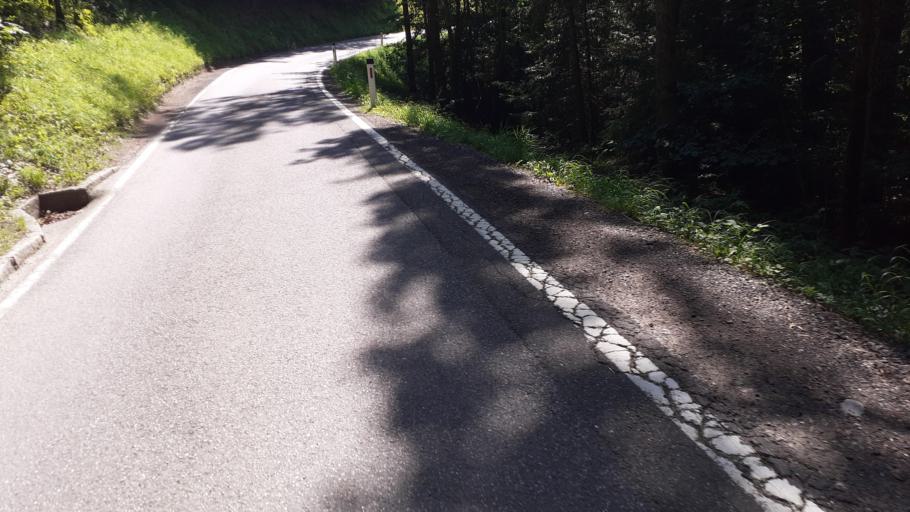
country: AT
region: Vorarlberg
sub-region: Politischer Bezirk Bregenz
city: Kennelbach
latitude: 47.4752
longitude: 9.7791
